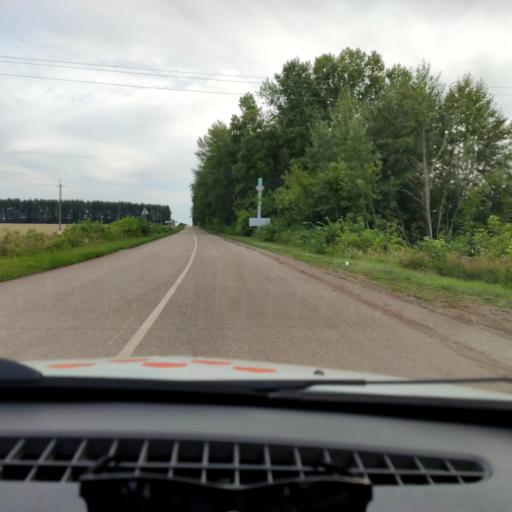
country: RU
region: Bashkortostan
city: Avdon
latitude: 54.5245
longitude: 55.6363
